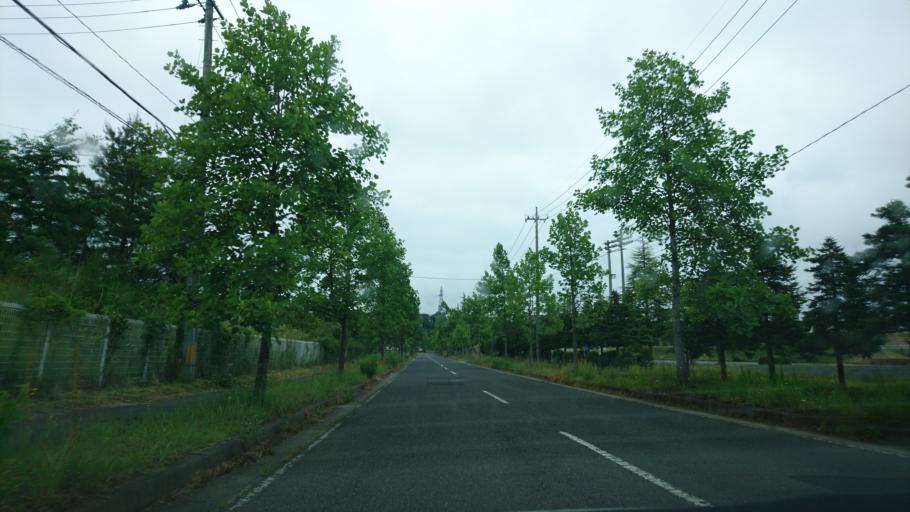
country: JP
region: Iwate
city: Ichinoseki
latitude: 38.9211
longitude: 141.1570
